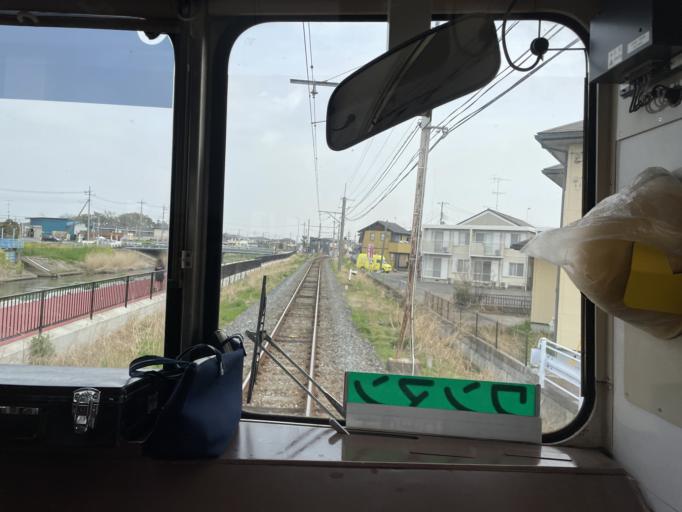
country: JP
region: Saitama
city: Gyoda
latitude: 36.1426
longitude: 139.4501
